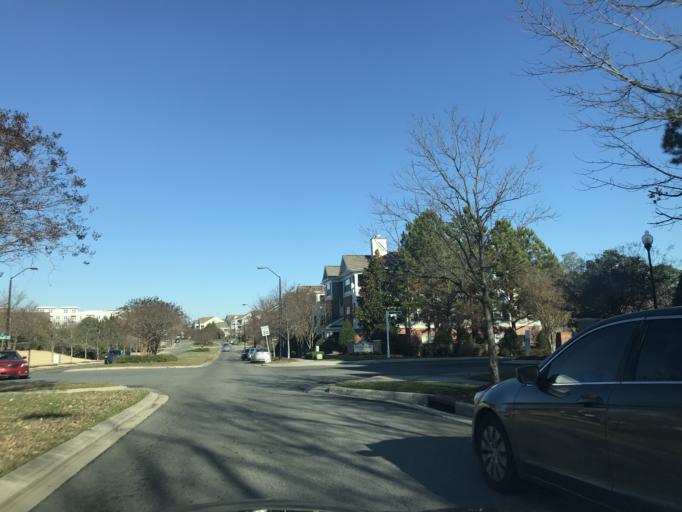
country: US
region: North Carolina
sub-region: Wake County
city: Morrisville
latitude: 35.8971
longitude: -78.8011
